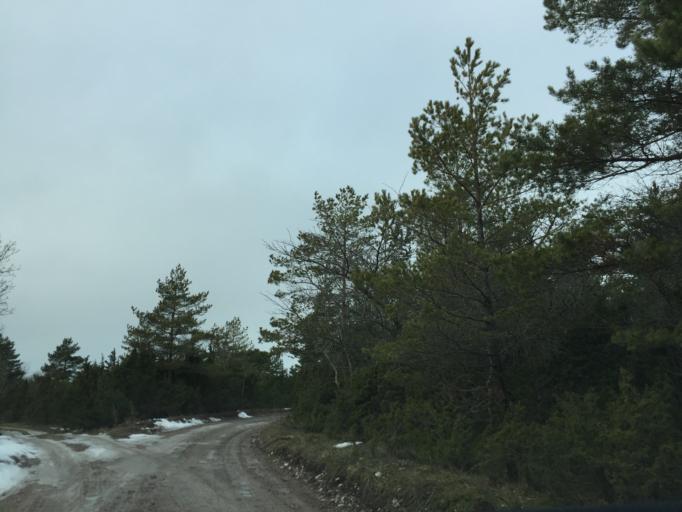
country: EE
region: Saare
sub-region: Kuressaare linn
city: Kuressaare
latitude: 58.4964
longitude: 21.9281
